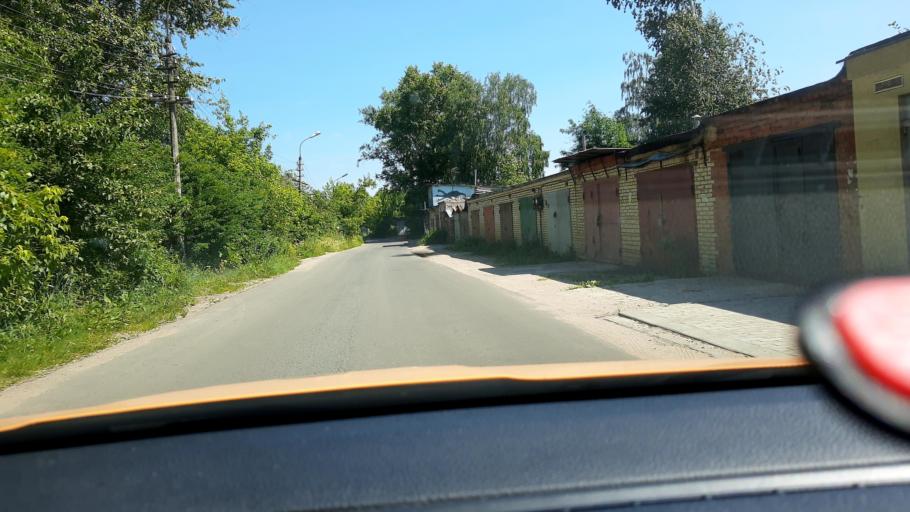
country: RU
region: Moscow
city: Severnyy
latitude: 55.9478
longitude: 37.5293
